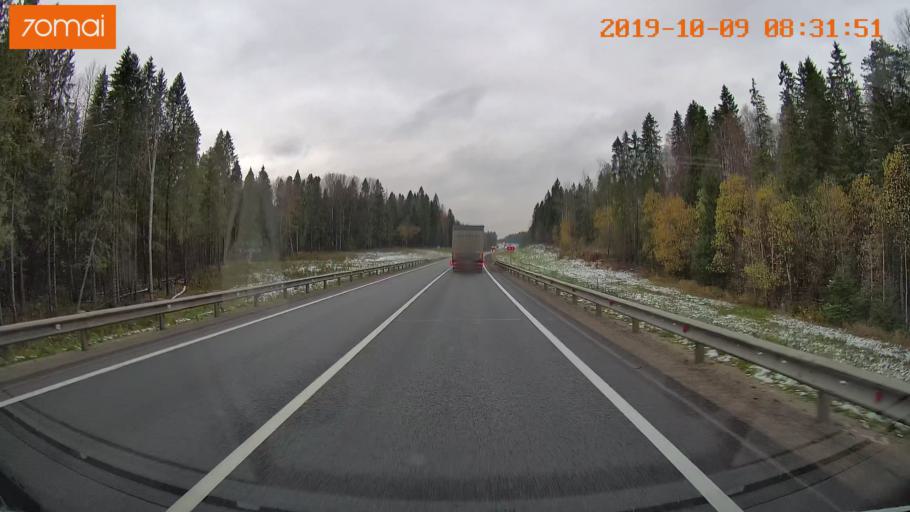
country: RU
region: Vologda
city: Gryazovets
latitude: 58.8592
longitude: 40.1994
